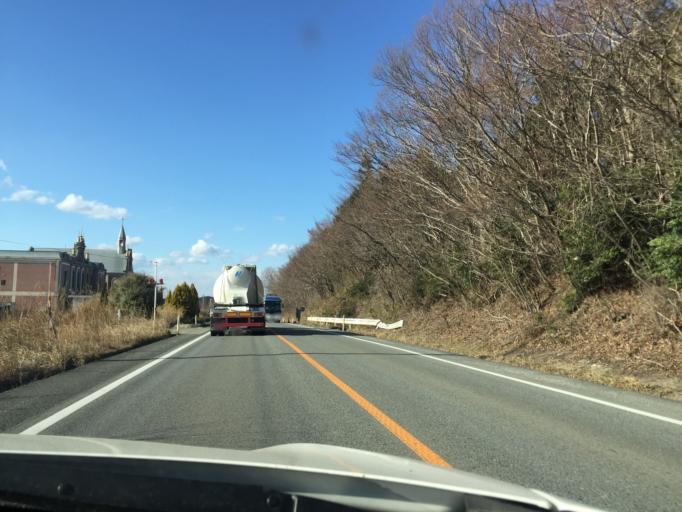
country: JP
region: Fukushima
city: Namie
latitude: 37.4769
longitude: 141.0075
